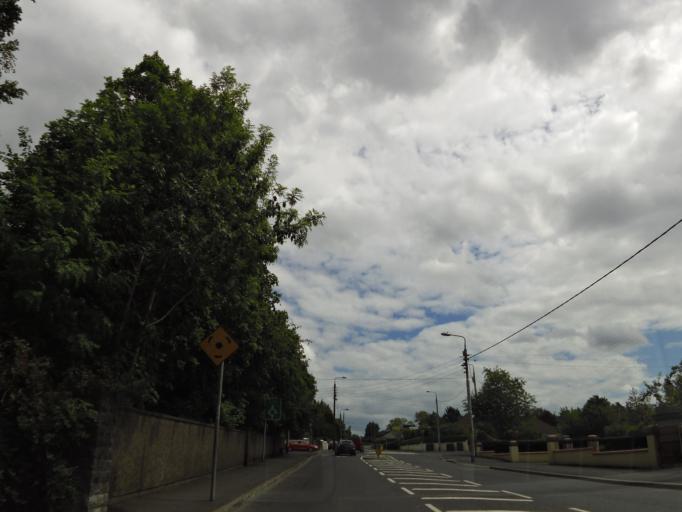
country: IE
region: Munster
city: Thurles
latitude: 52.6798
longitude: -7.7994
